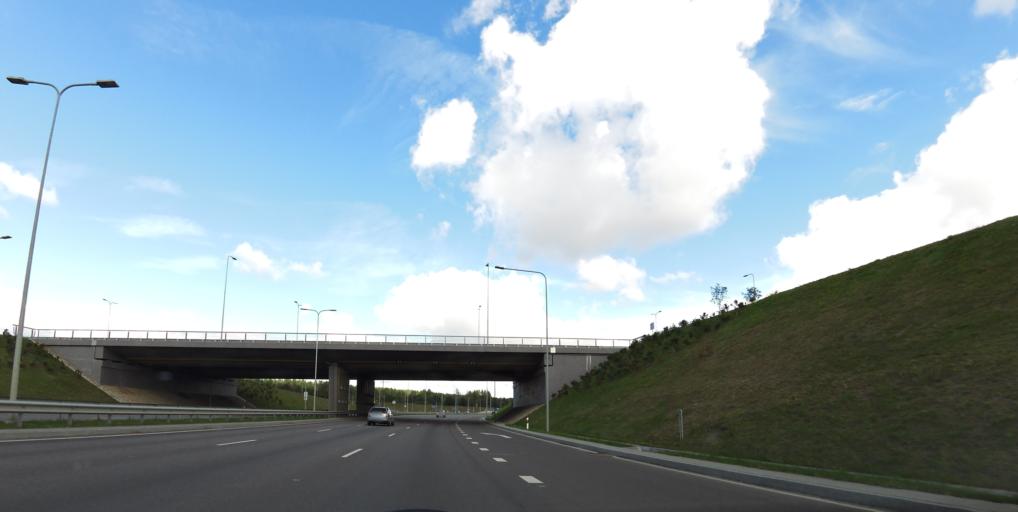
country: LT
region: Vilnius County
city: Lazdynai
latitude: 54.6824
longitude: 25.1946
